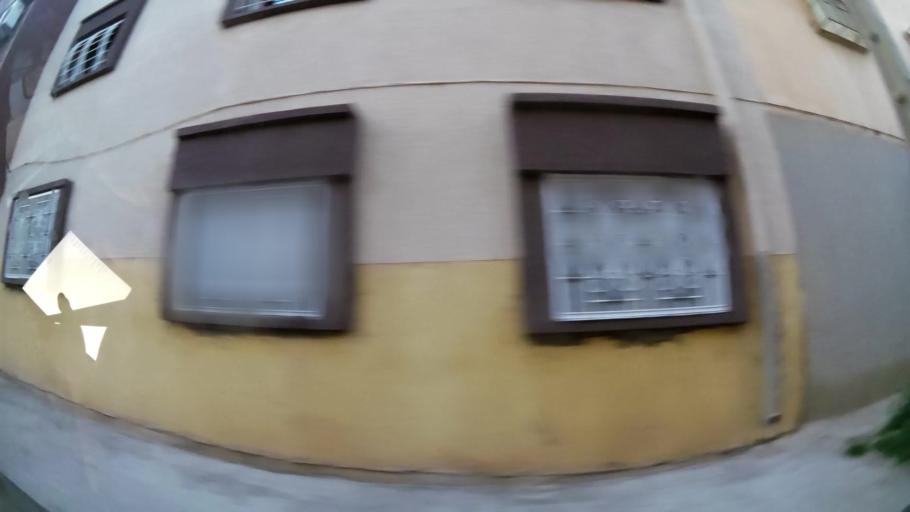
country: MA
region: Oriental
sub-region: Oujda-Angad
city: Oujda
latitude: 34.6813
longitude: -1.8783
